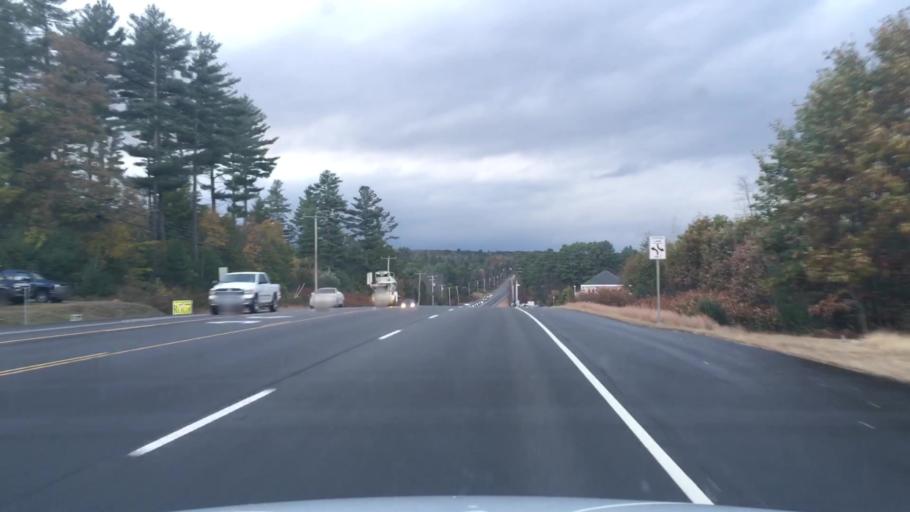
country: US
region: New Hampshire
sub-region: Merrimack County
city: Epsom
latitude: 43.2294
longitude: -71.3658
